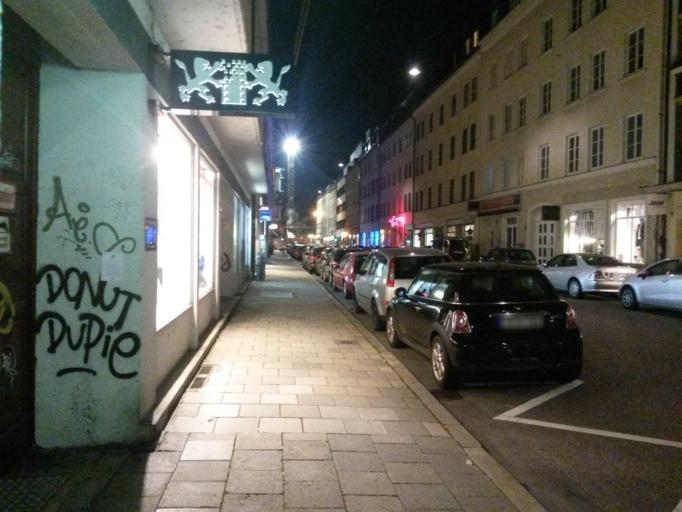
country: DE
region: Bavaria
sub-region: Upper Bavaria
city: Munich
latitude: 48.1295
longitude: 11.5758
